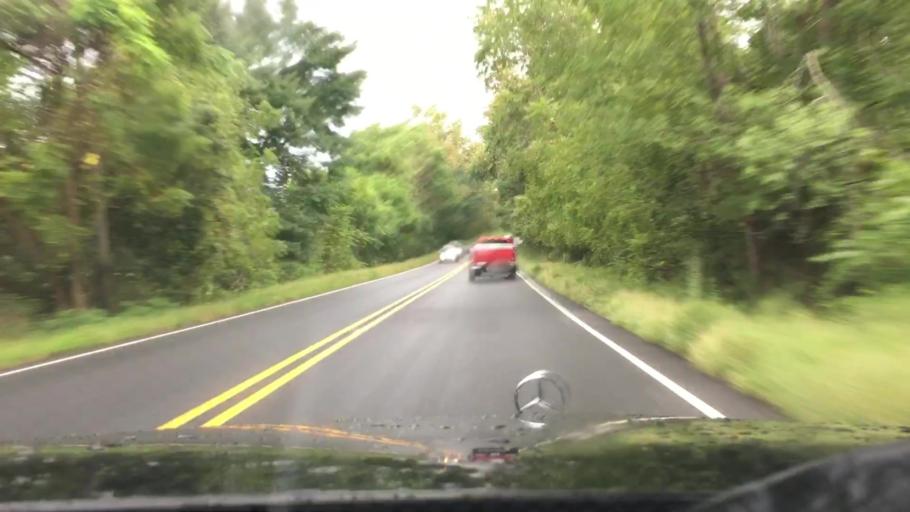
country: US
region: Virginia
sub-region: Nelson County
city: Nellysford
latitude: 37.9010
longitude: -78.8584
